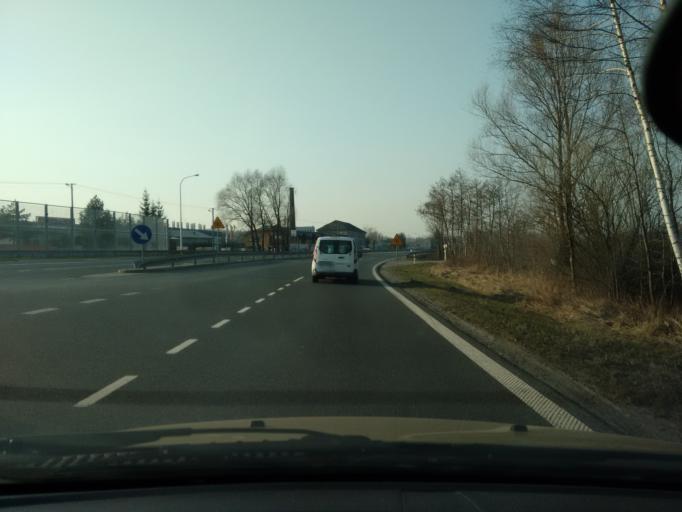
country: PL
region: Silesian Voivodeship
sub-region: Powiat cieszynski
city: Skoczow
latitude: 49.7923
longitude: 18.7974
